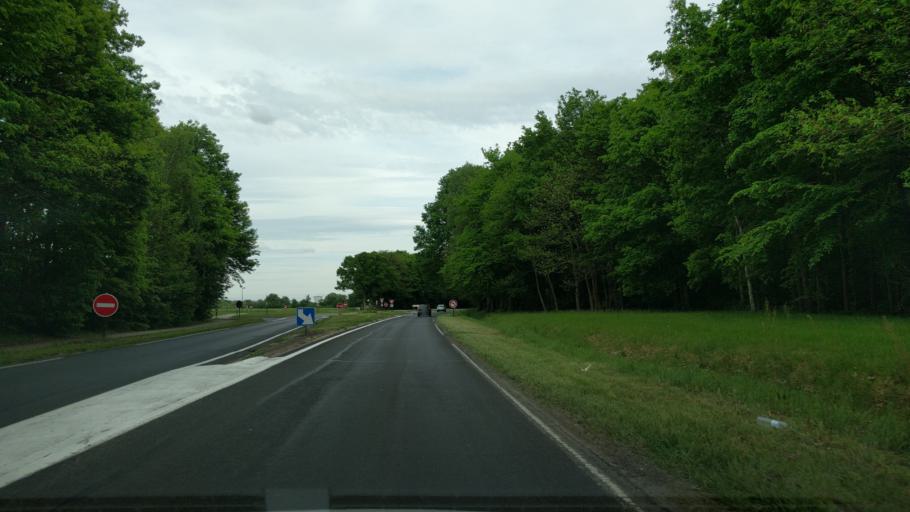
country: FR
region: Ile-de-France
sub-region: Departement de Seine-et-Marne
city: Seine-Port
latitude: 48.5544
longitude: 2.5679
